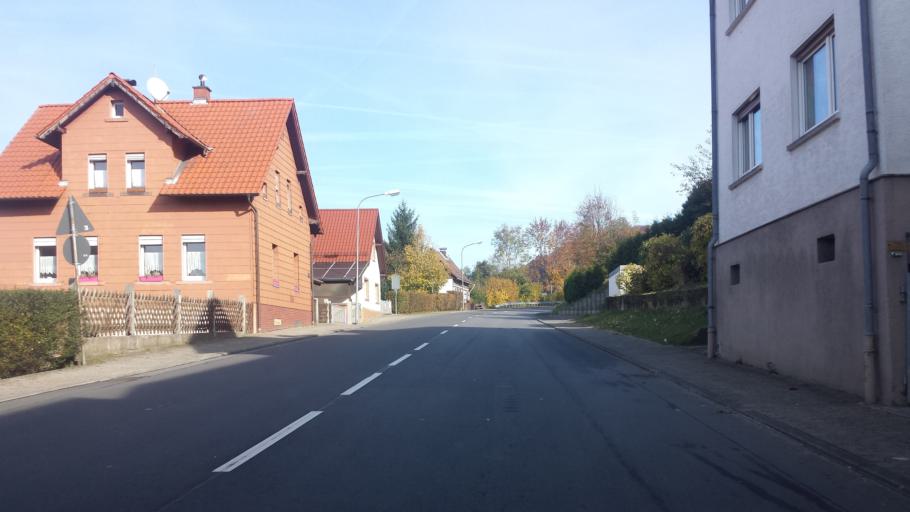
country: DE
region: Hesse
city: Lutzelbach
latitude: 49.7190
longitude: 8.7180
